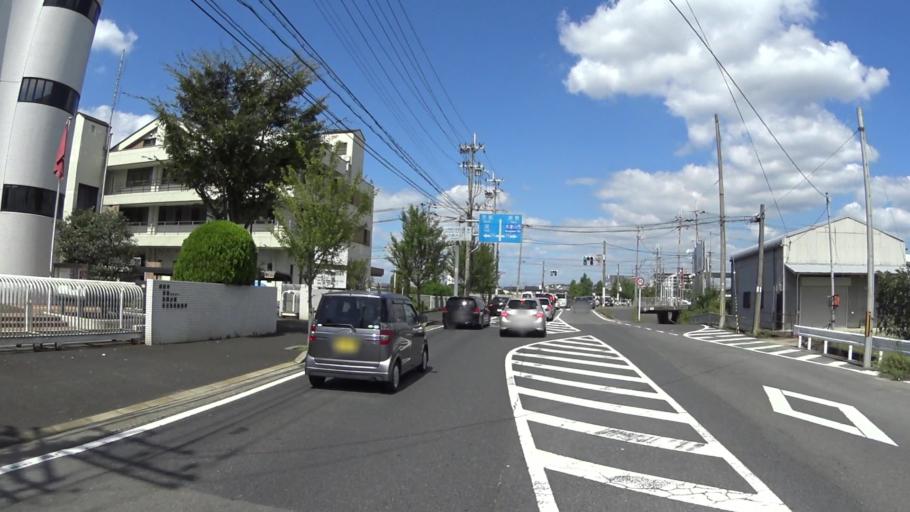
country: JP
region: Kyoto
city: Tanabe
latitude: 34.8461
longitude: 135.7802
